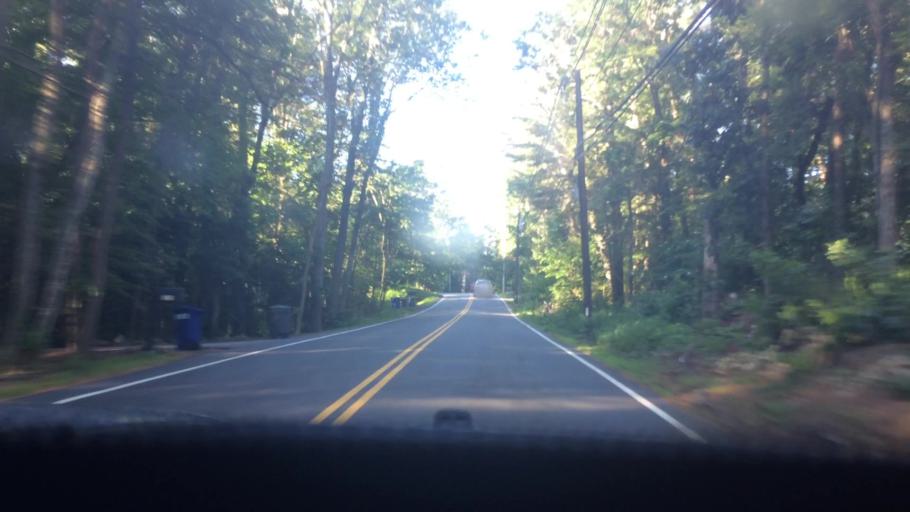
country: US
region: Massachusetts
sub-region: Essex County
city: Andover
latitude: 42.6290
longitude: -71.0925
